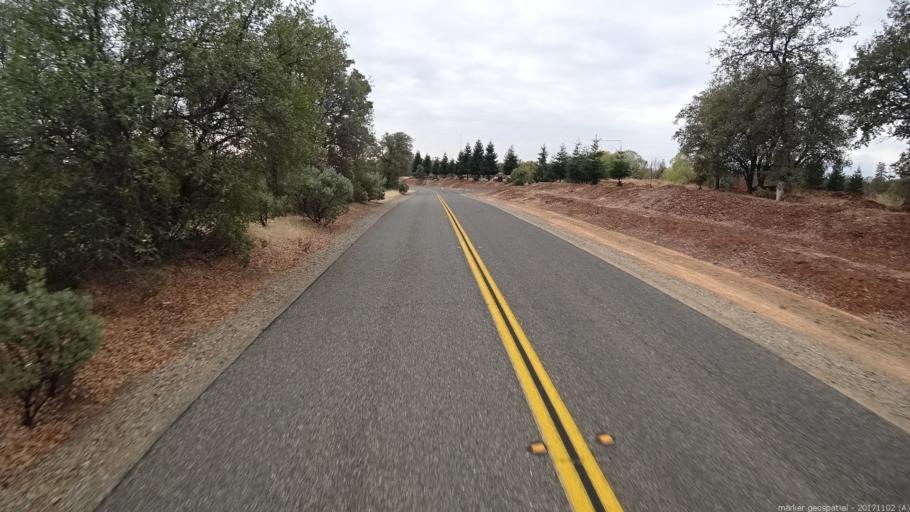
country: US
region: California
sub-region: Shasta County
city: Redding
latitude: 40.6272
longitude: -122.4315
